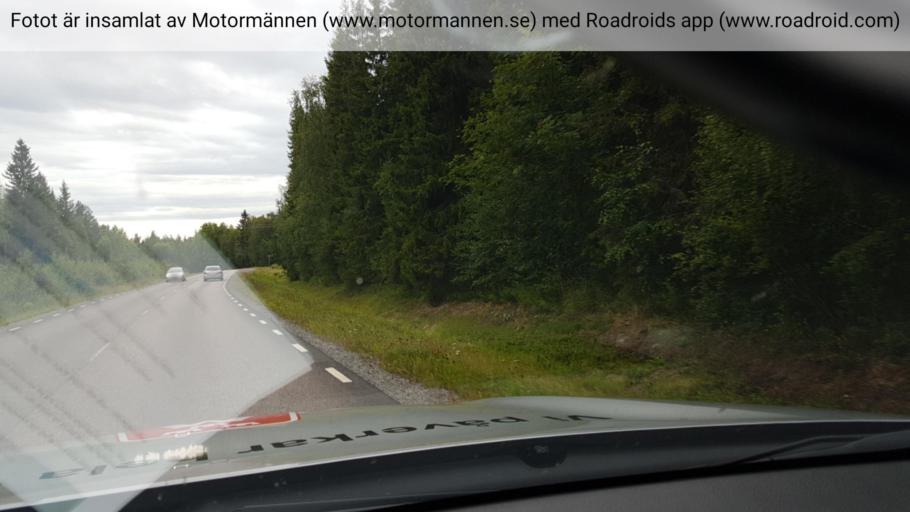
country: SE
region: Norrbotten
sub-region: Lulea Kommun
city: Gammelstad
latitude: 65.6551
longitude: 22.0369
